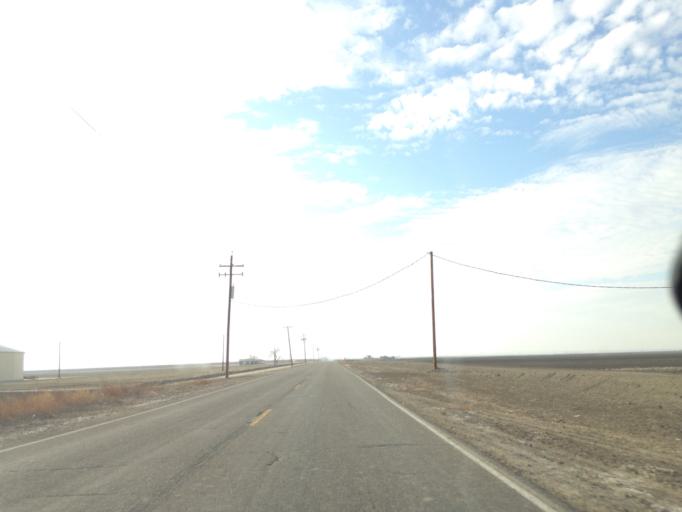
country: US
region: California
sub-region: Kern County
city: Buttonwillow
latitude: 35.4419
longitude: -119.5301
